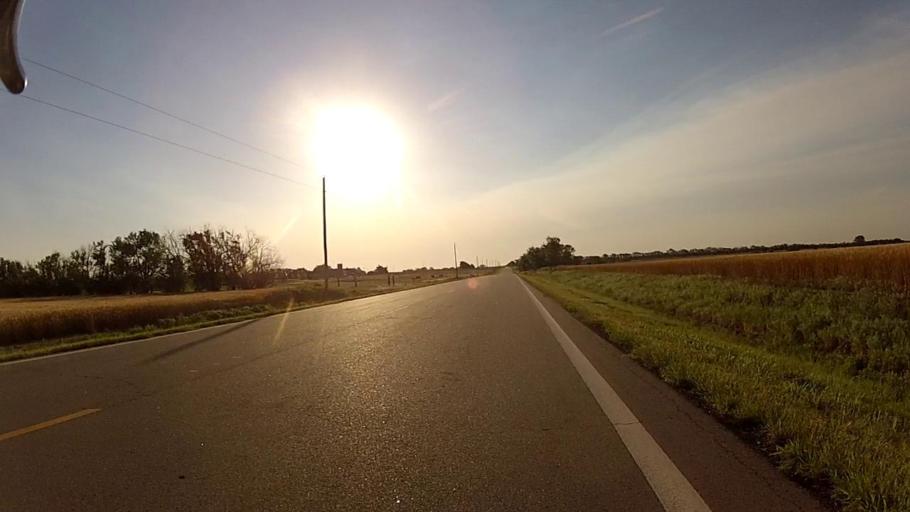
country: US
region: Kansas
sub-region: Sumner County
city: Caldwell
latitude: 37.1540
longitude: -97.7900
